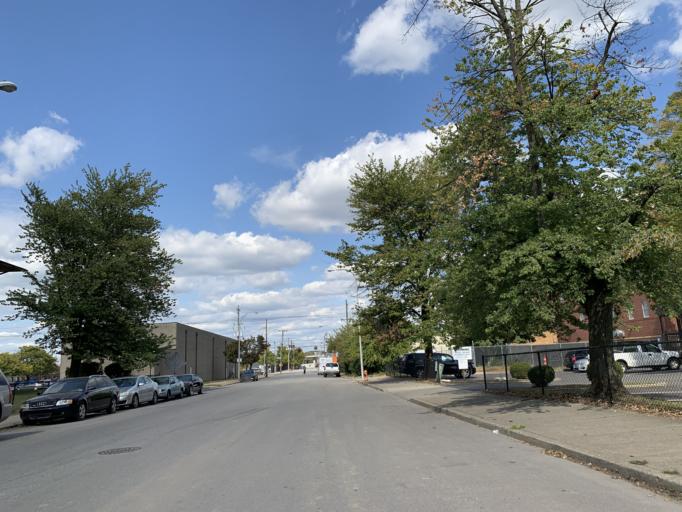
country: US
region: Kentucky
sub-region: Jefferson County
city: Louisville
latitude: 38.2553
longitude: -85.7685
